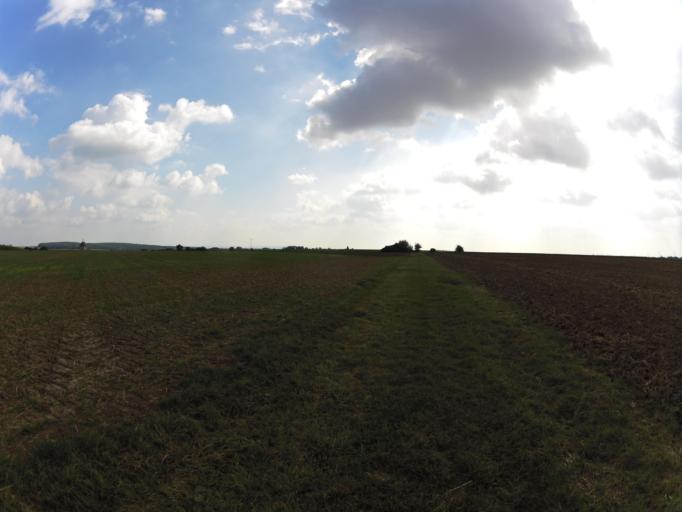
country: DE
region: Bavaria
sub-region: Regierungsbezirk Unterfranken
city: Prosselsheim
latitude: 49.8662
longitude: 10.1136
